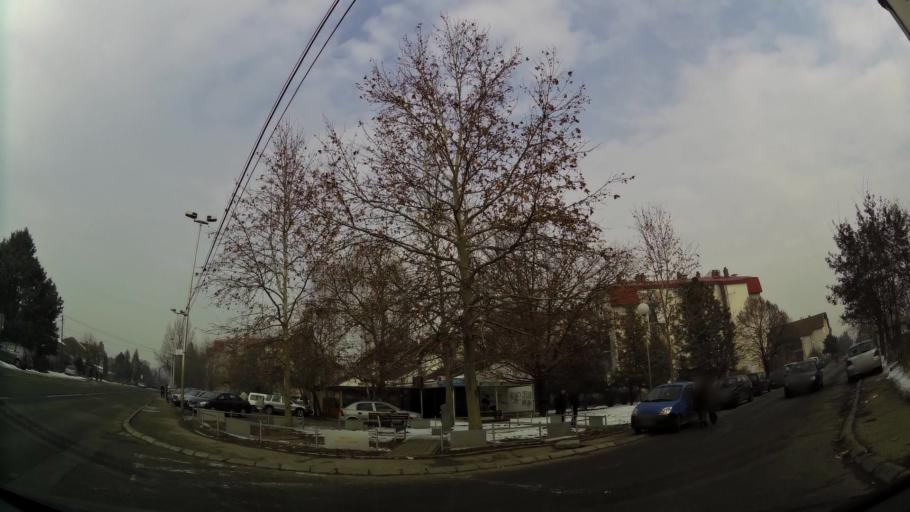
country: MK
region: Saraj
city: Saraj
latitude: 42.0204
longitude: 21.3526
